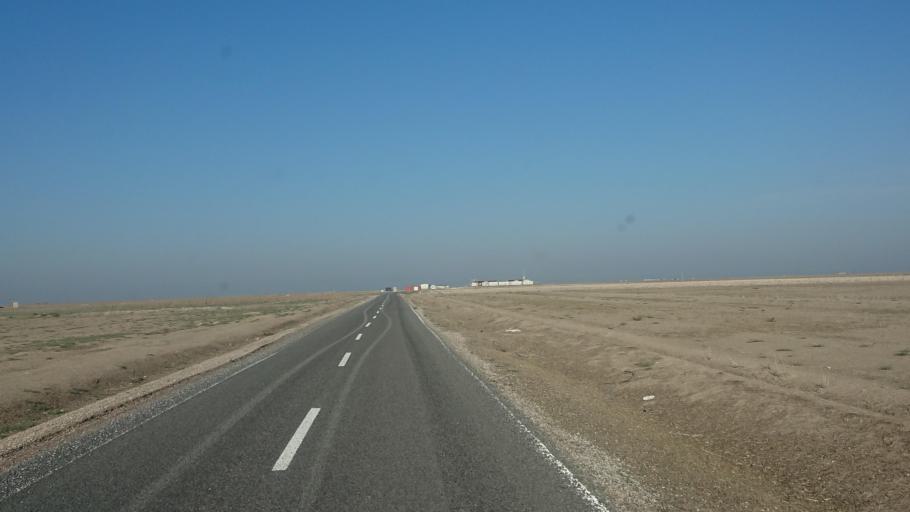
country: TR
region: Aksaray
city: Yesilova
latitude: 38.3879
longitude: 33.7541
